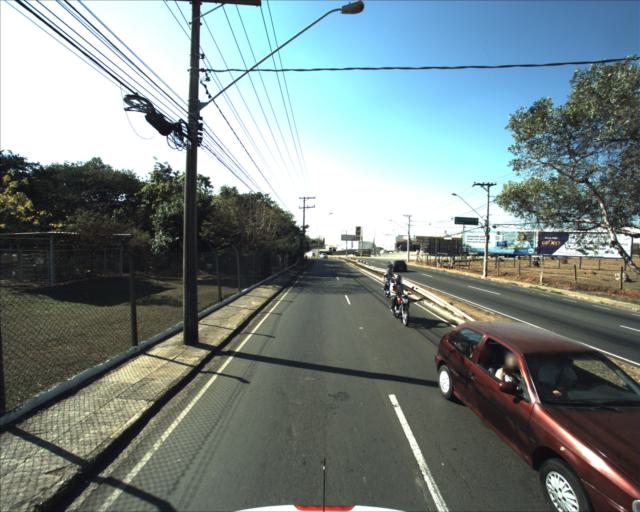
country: BR
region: Sao Paulo
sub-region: Sorocaba
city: Sorocaba
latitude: -23.4563
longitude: -47.4192
